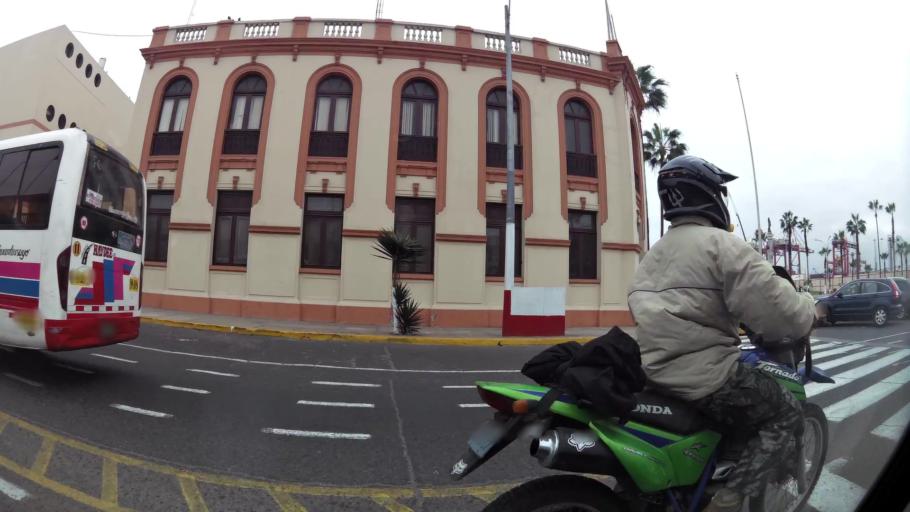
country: PE
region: Callao
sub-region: Callao
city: Callao
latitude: -12.0598
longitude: -77.1488
